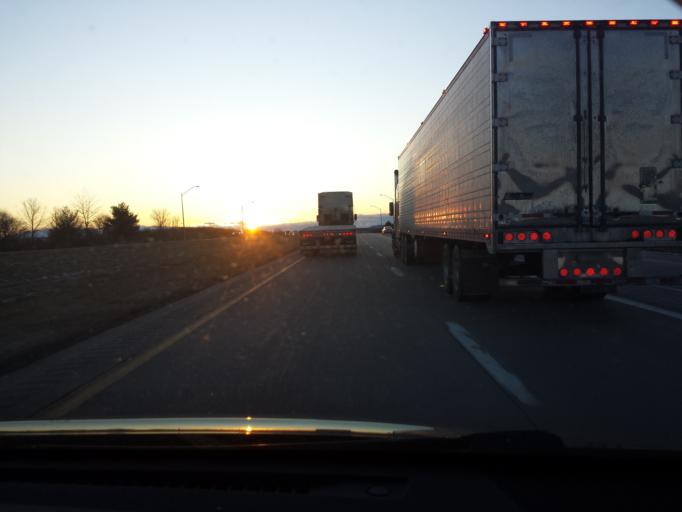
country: US
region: Pennsylvania
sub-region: Centre County
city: Pleasant Gap
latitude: 40.8837
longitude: -77.7442
